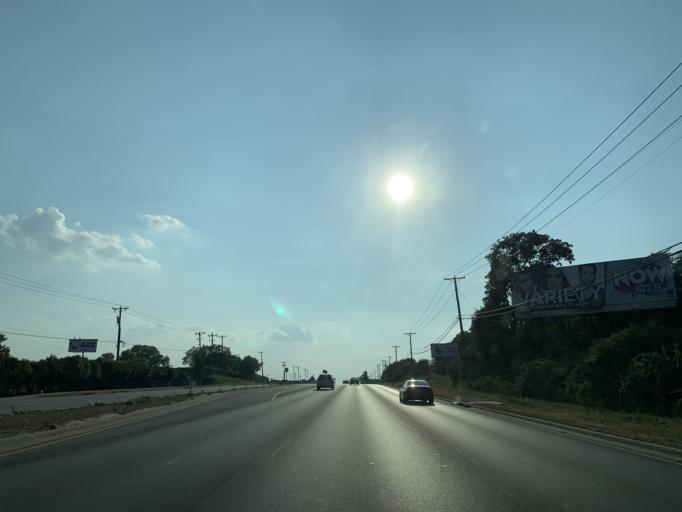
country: US
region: Texas
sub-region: Tarrant County
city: Hurst
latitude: 32.8091
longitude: -97.1796
